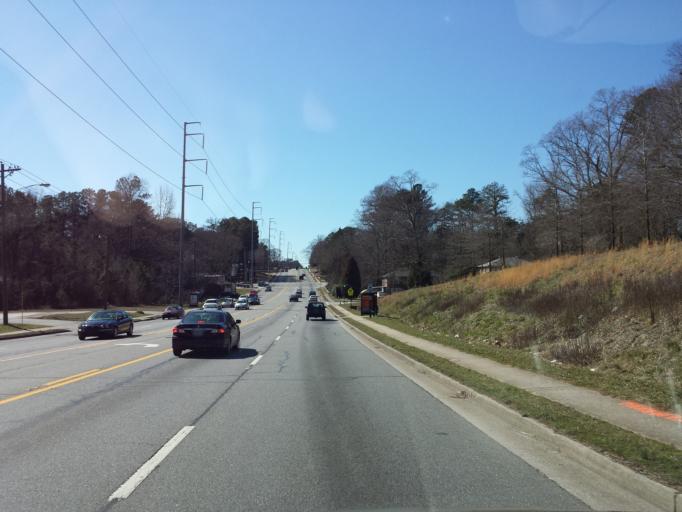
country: US
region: Georgia
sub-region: Cobb County
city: Fair Oaks
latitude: 33.8948
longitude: -84.5551
